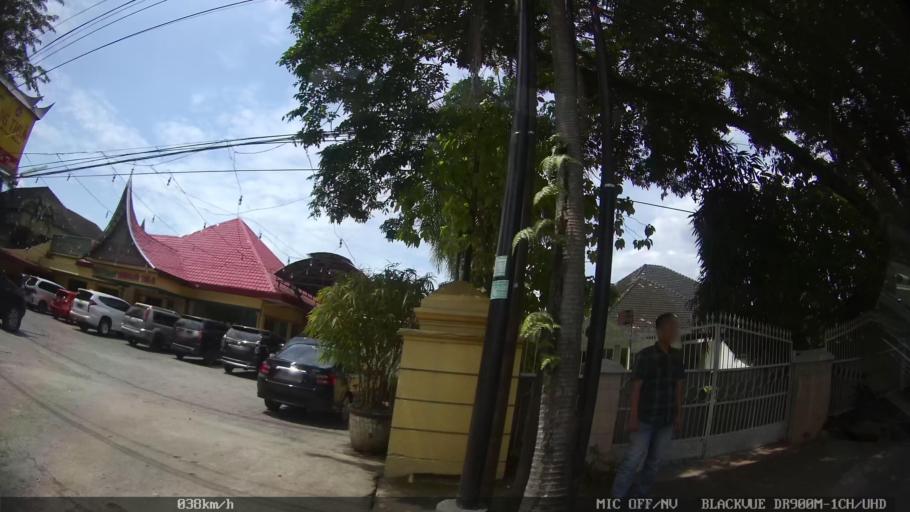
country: ID
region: North Sumatra
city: Medan
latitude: 3.5713
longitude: 98.6676
